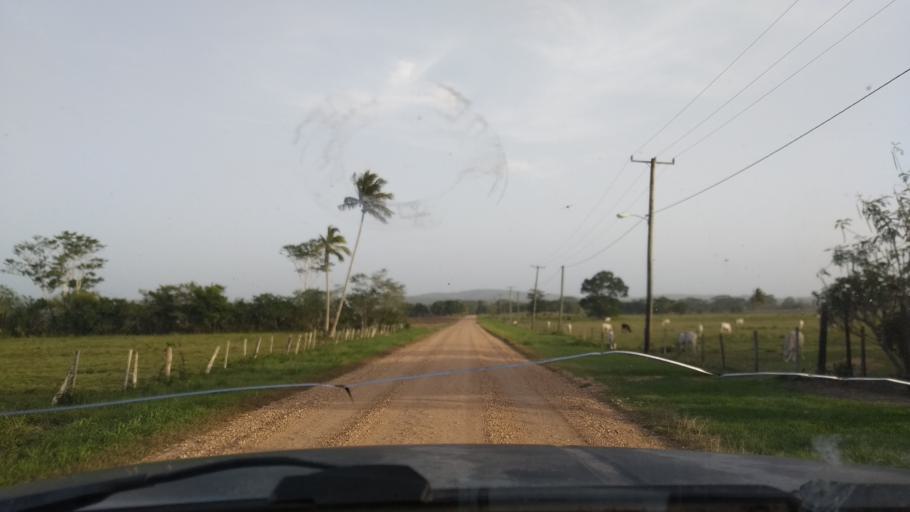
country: BZ
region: Cayo
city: San Ignacio
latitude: 17.2158
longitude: -89.0137
